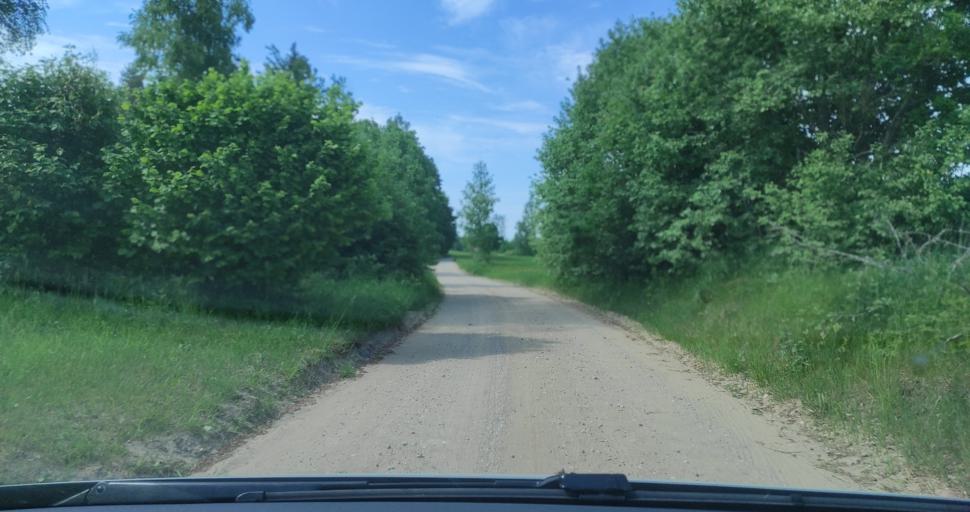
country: LV
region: Kuldigas Rajons
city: Kuldiga
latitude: 56.8568
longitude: 21.9091
